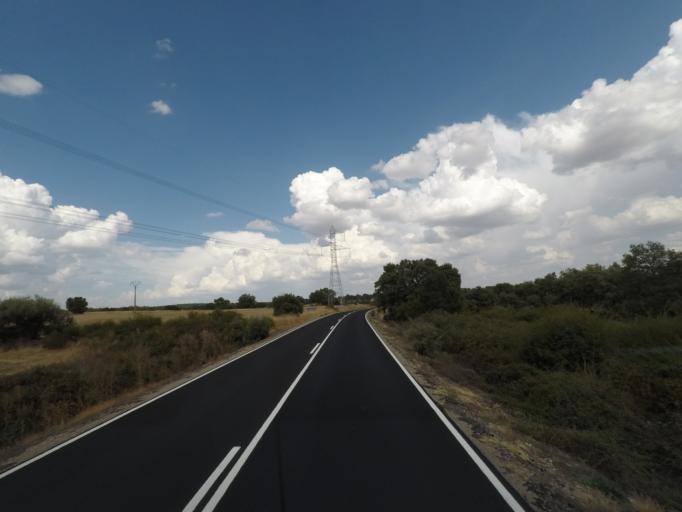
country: ES
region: Castille and Leon
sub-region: Provincia de Zamora
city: Fermoselle
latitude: 41.3013
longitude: -6.3256
